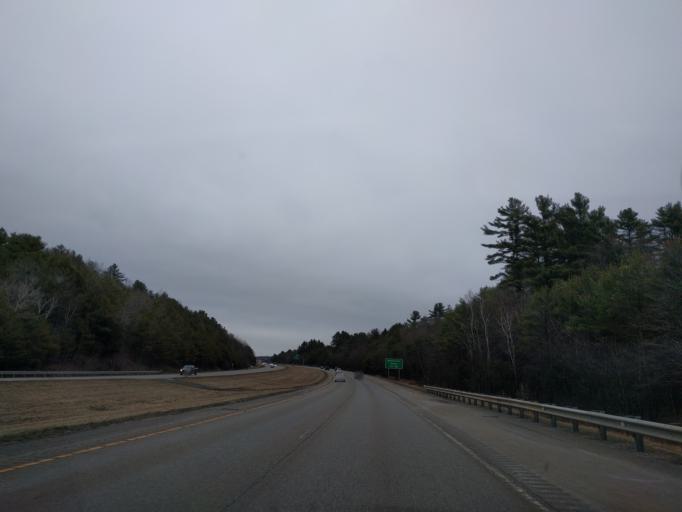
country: US
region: Massachusetts
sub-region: Worcester County
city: Gardner
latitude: 42.5591
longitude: -72.0107
